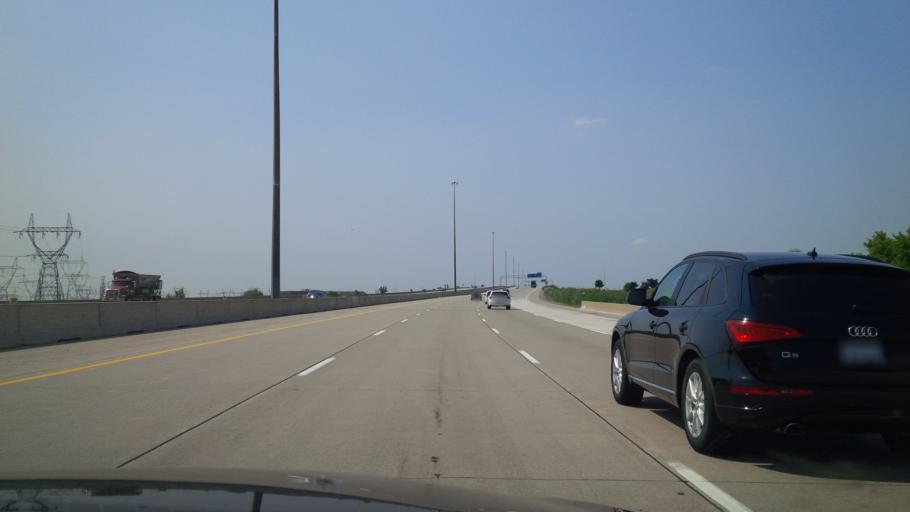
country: CA
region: Ontario
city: Brampton
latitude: 43.7111
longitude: -79.6767
